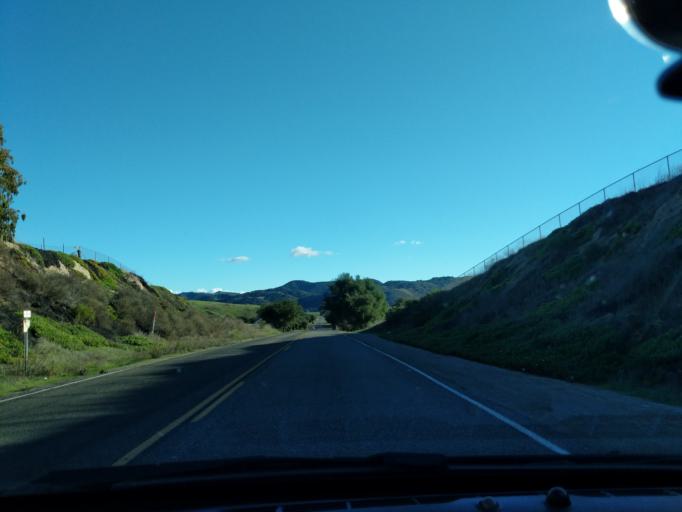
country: US
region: California
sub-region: Santa Barbara County
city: Los Alamos
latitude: 34.7549
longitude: -120.2951
